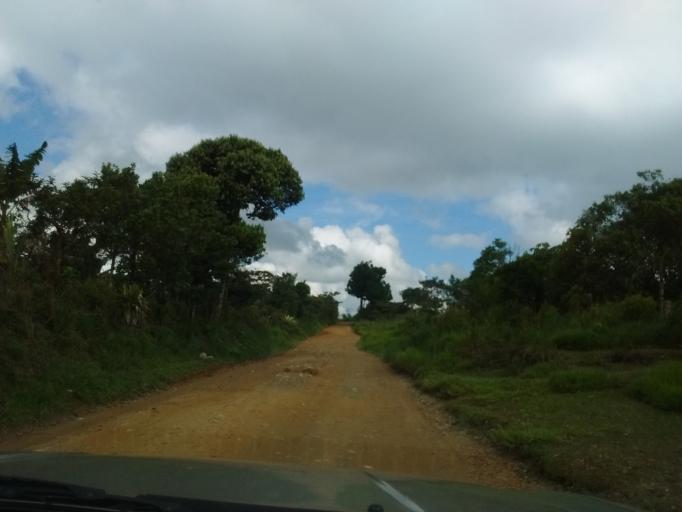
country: CO
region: Cauca
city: Cajibio
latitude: 2.6526
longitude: -76.6870
